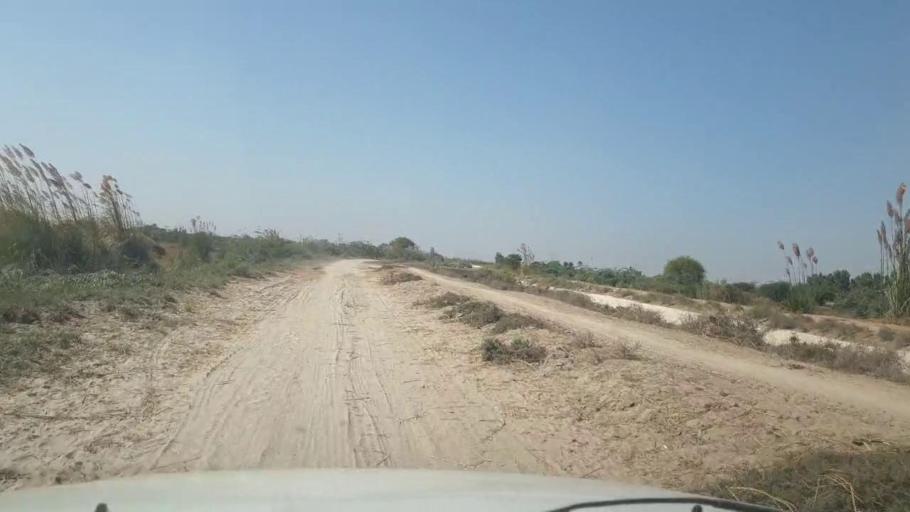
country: PK
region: Sindh
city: Chuhar Jamali
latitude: 24.4230
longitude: 67.7925
